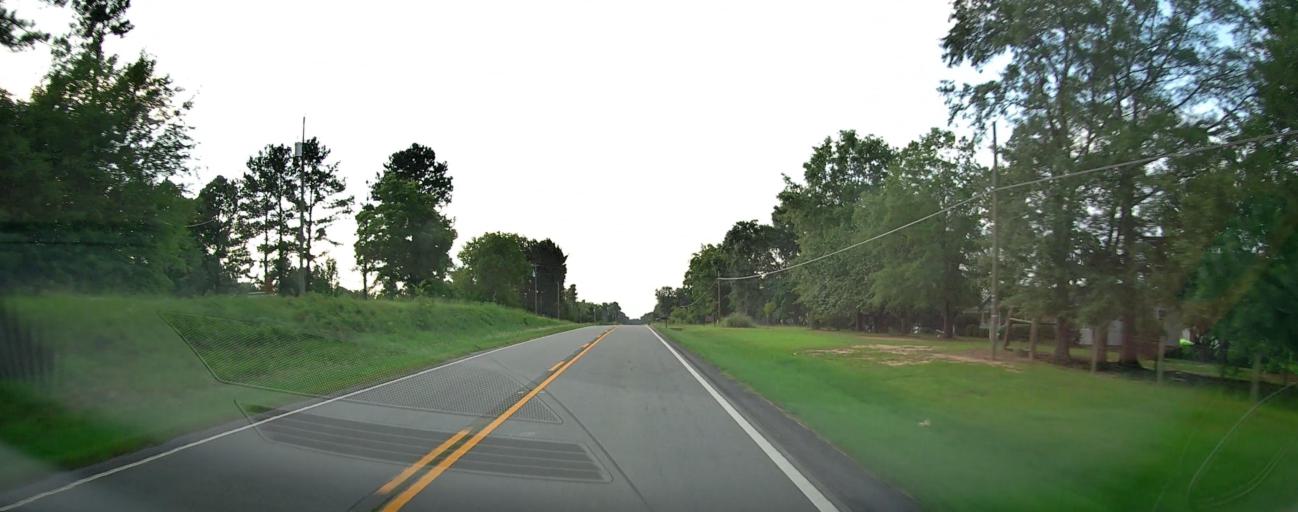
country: US
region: Georgia
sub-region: Taylor County
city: Reynolds
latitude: 32.6033
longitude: -84.0951
